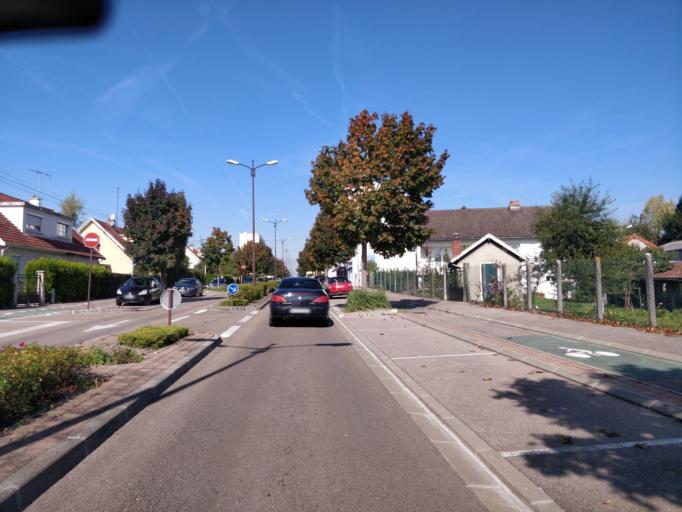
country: FR
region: Champagne-Ardenne
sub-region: Departement de l'Aube
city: Rosieres-pres-Troyes
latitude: 48.2761
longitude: 4.0779
